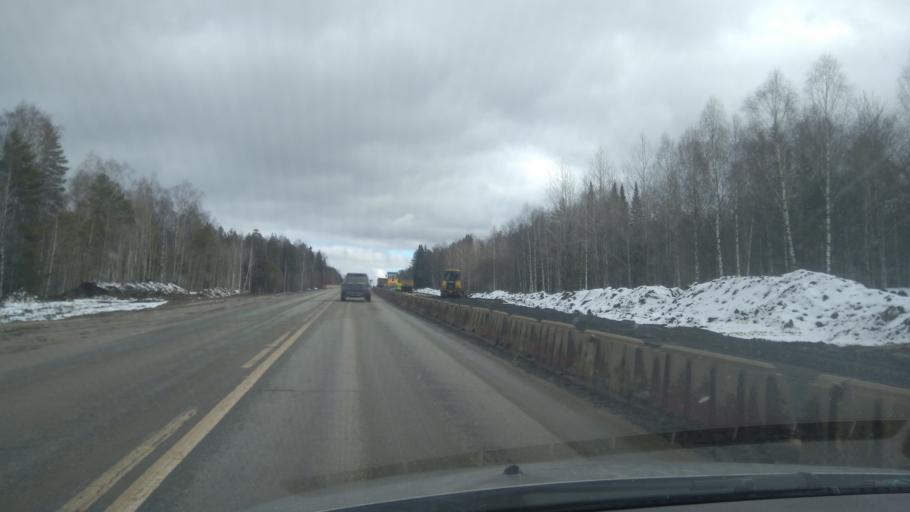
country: RU
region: Sverdlovsk
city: Bisert'
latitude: 56.8341
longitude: 58.9358
